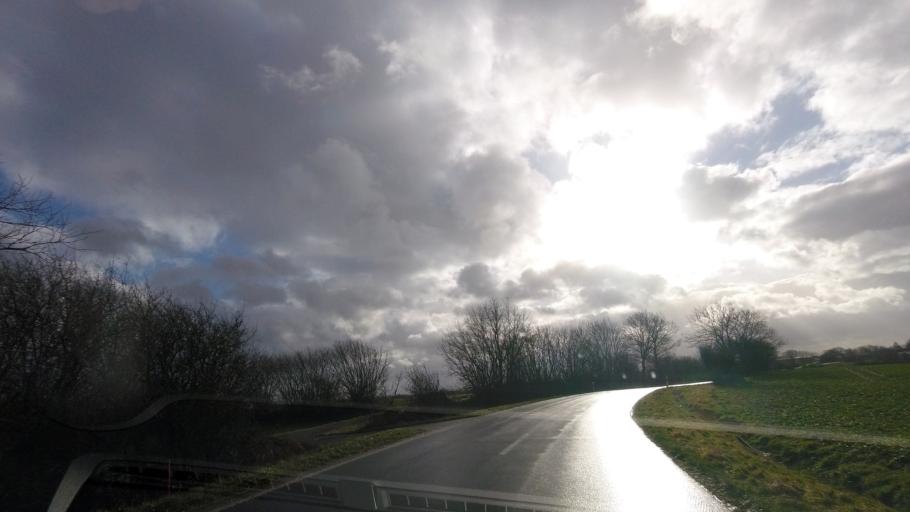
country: DE
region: Schleswig-Holstein
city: Grodersby
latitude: 54.6458
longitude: 9.9193
